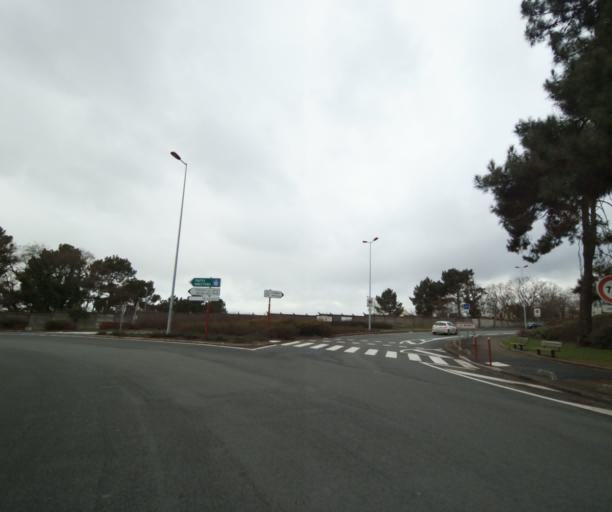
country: FR
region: Pays de la Loire
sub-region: Departement de la Sarthe
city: Arnage
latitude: 47.9573
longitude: 0.1990
